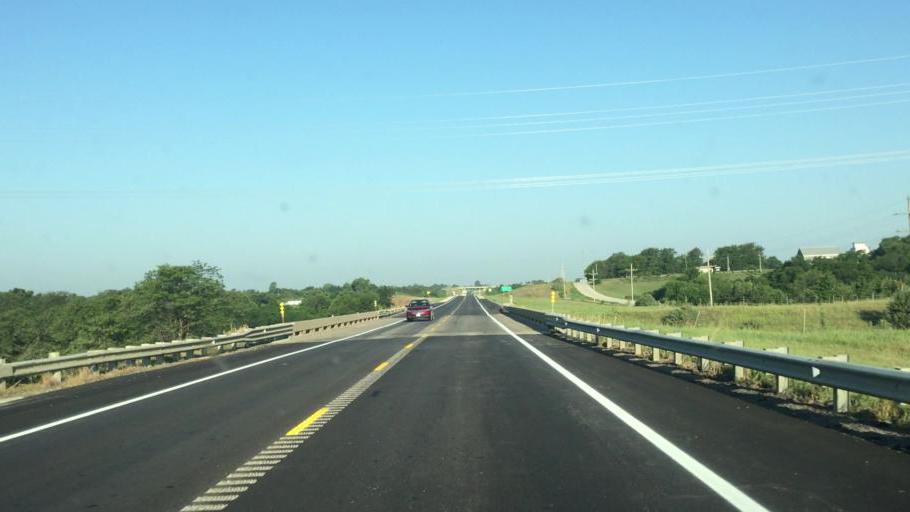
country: US
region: Kansas
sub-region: Brown County
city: Hiawatha
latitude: 39.8413
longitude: -95.4700
